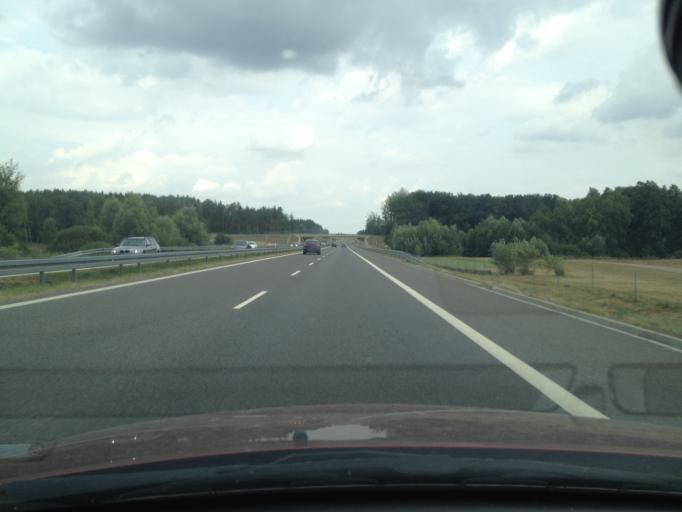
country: PL
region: West Pomeranian Voivodeship
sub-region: Powiat mysliborski
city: Mysliborz
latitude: 53.0075
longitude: 14.8618
